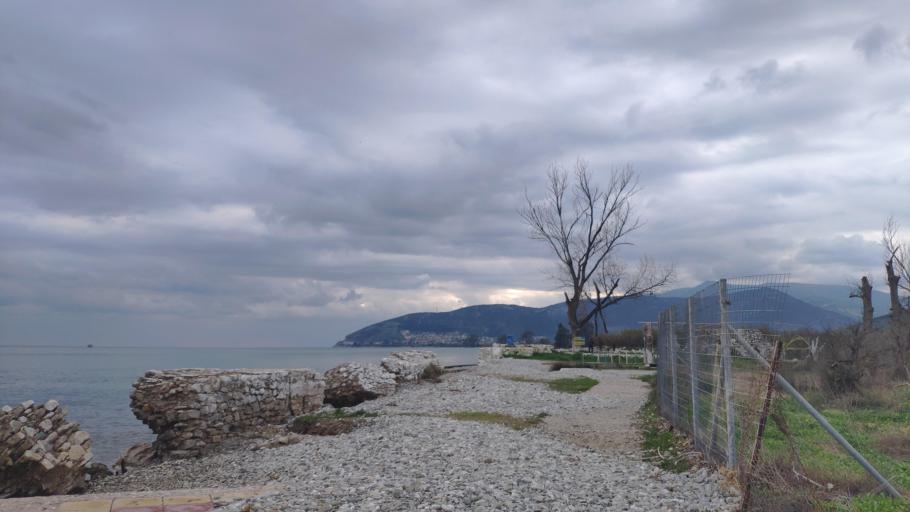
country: GR
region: Peloponnese
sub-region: Nomos Argolidos
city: Nea Kios
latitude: 37.5532
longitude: 22.7205
